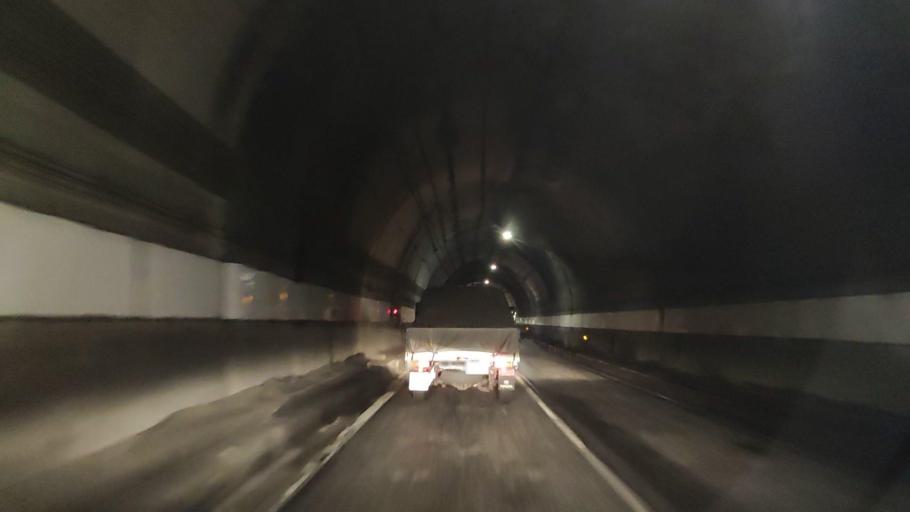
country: JP
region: Nagano
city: Toyoshina
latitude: 36.1449
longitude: 137.6944
